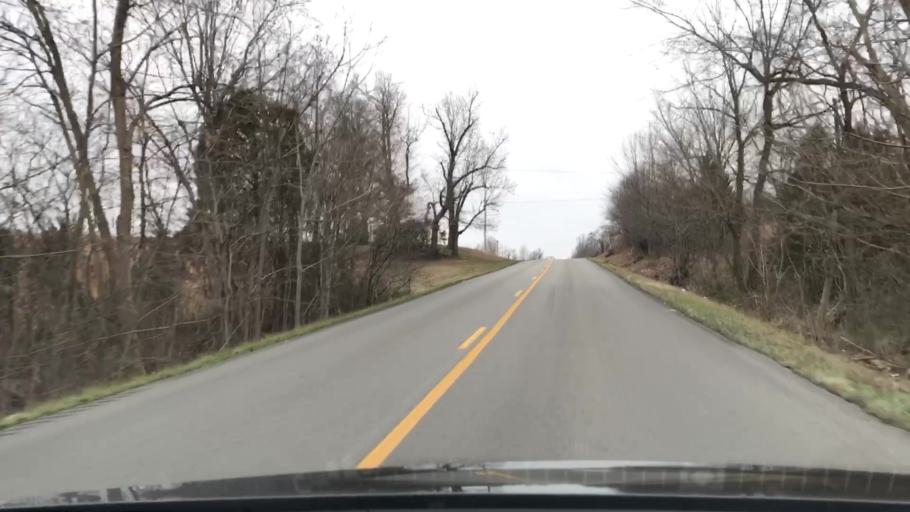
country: US
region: Kentucky
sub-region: Muhlenberg County
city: Morehead
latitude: 37.3185
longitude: -87.2182
